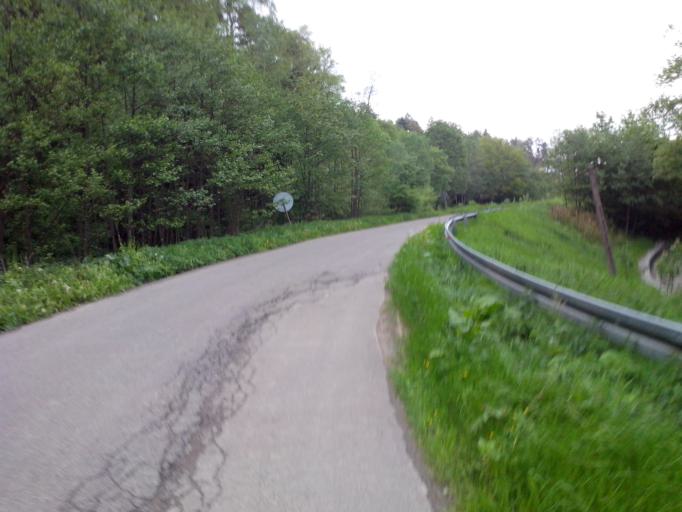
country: PL
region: Subcarpathian Voivodeship
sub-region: Powiat strzyzowski
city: Strzyzow
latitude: 49.8078
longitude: 21.8255
